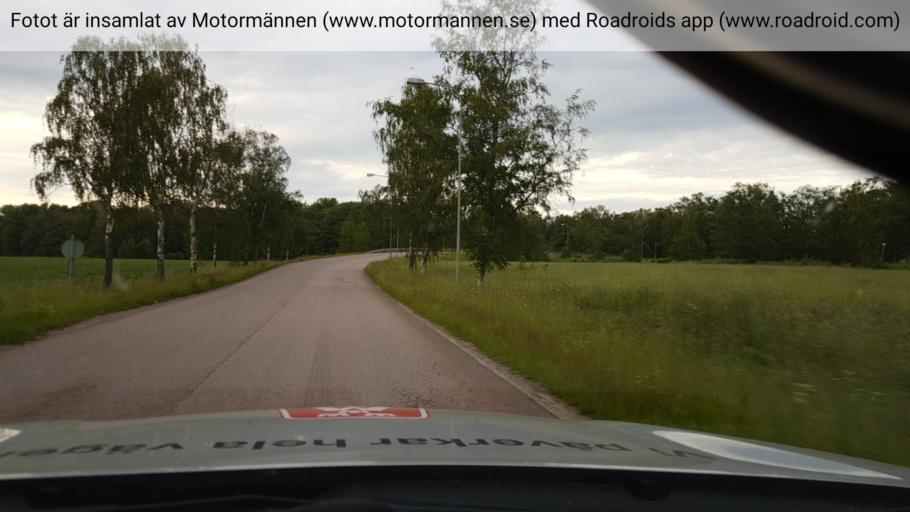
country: SE
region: Vaestmanland
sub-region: Surahammars Kommun
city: Surahammar
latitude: 59.7106
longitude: 16.2065
